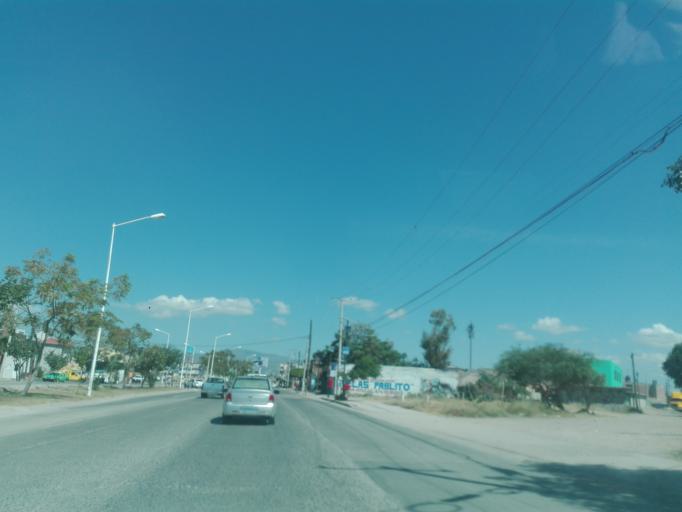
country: MX
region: Guanajuato
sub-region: Leon
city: San Jose de Duran (Los Troncoso)
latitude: 21.0770
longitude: -101.6348
